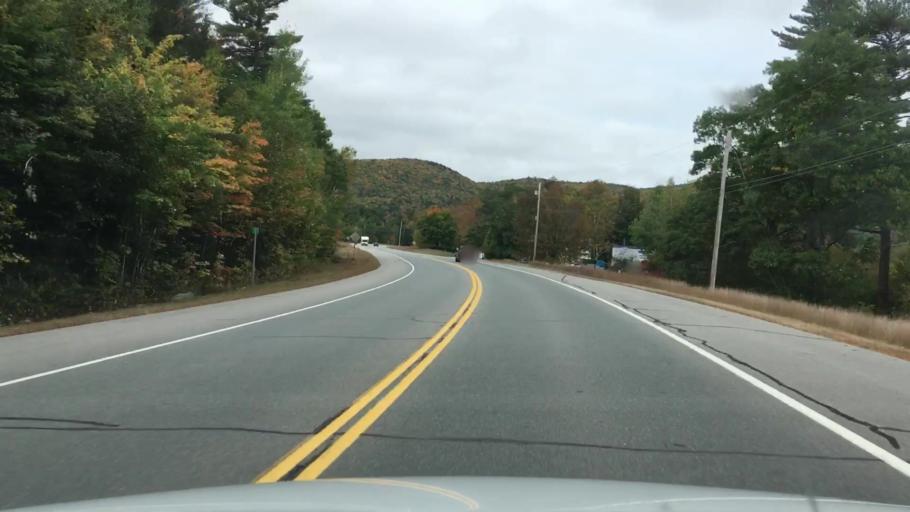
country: US
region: New Hampshire
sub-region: Coos County
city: Gorham
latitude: 44.3984
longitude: -71.0608
